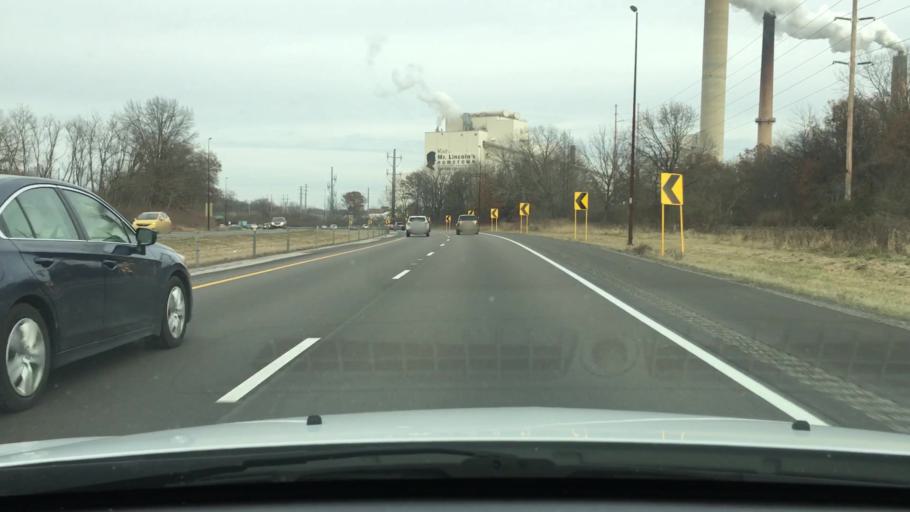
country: US
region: Illinois
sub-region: Sangamon County
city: Southern View
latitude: 39.7531
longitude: -89.6100
